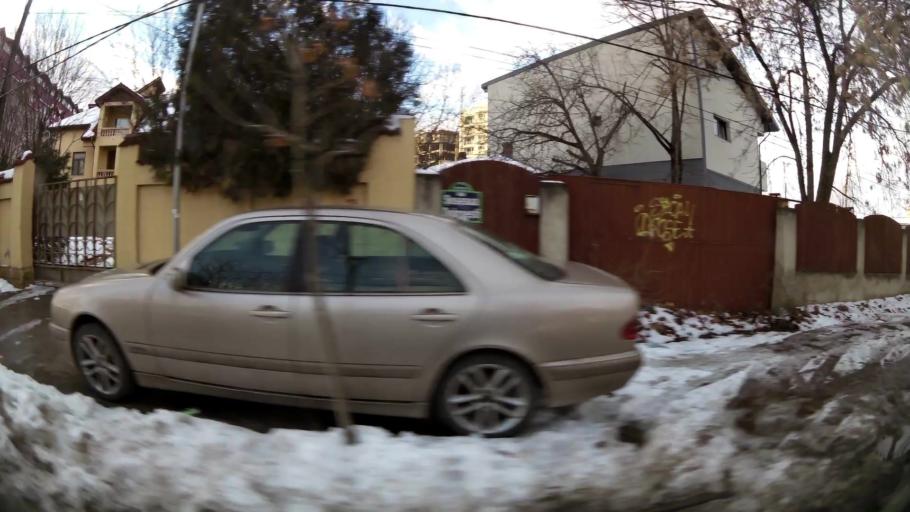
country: RO
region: Ilfov
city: Dobroesti
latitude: 44.4479
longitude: 26.1725
